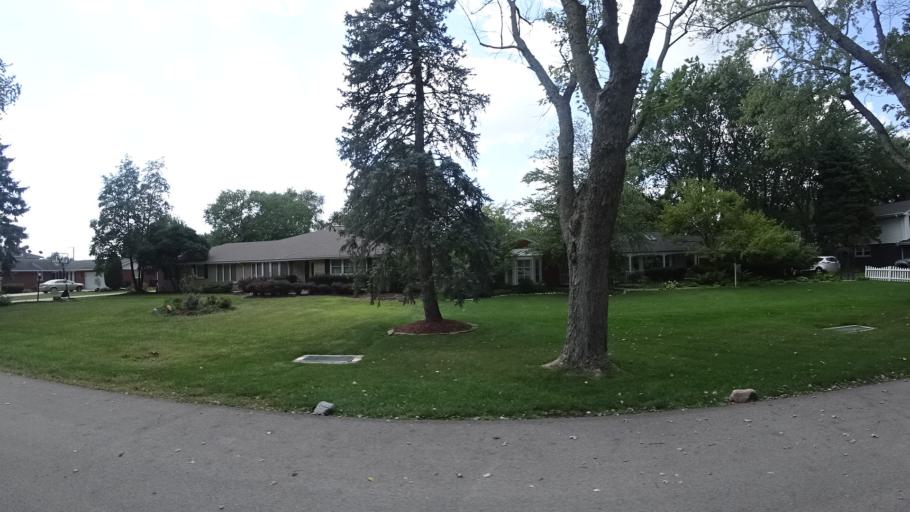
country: US
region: Illinois
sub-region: Cook County
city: Orland Park
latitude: 41.6176
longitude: -87.8159
